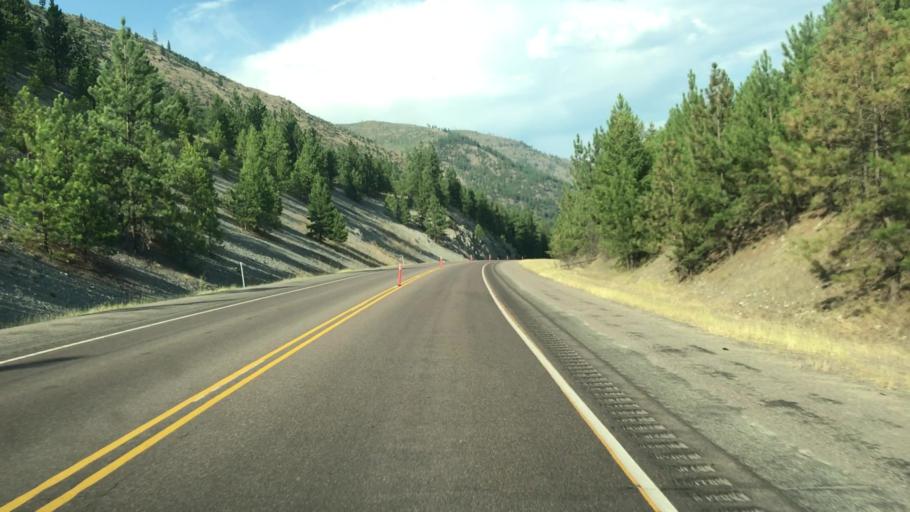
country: US
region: Montana
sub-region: Mineral County
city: Superior
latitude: 47.0159
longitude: -114.6907
